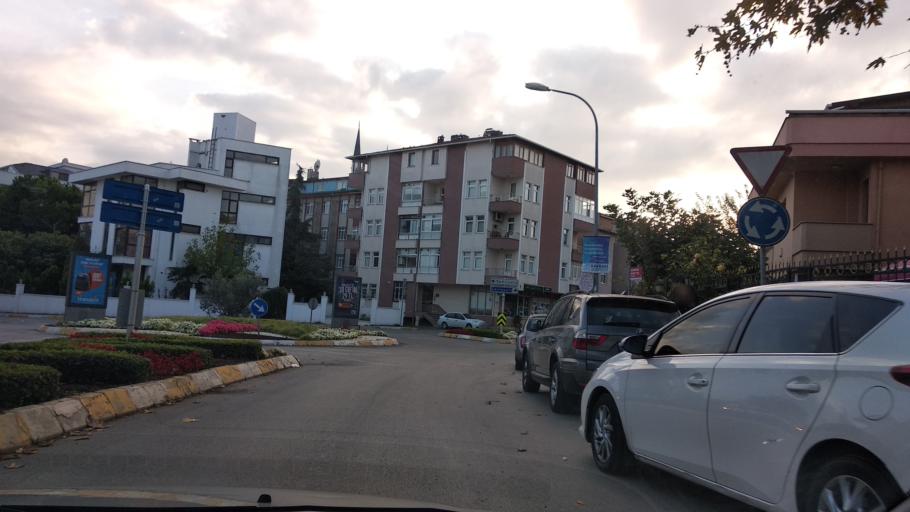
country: TR
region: Istanbul
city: Icmeler
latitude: 40.8193
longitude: 29.2986
